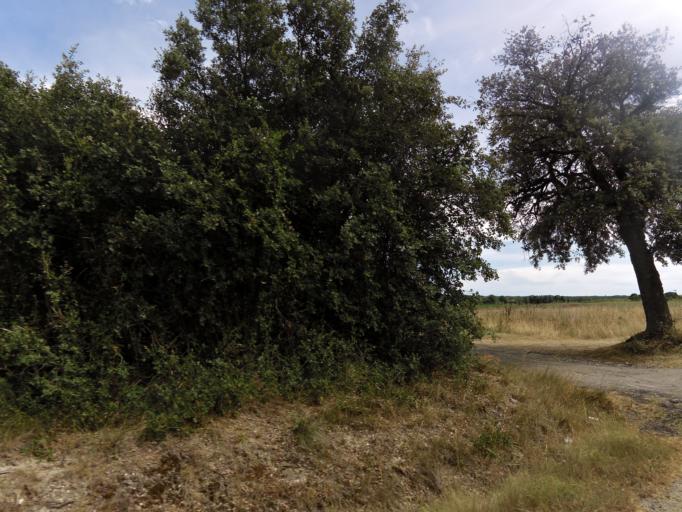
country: FR
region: Languedoc-Roussillon
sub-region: Departement du Gard
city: Saint-Mamert-du-Gard
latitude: 43.8666
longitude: 4.1641
